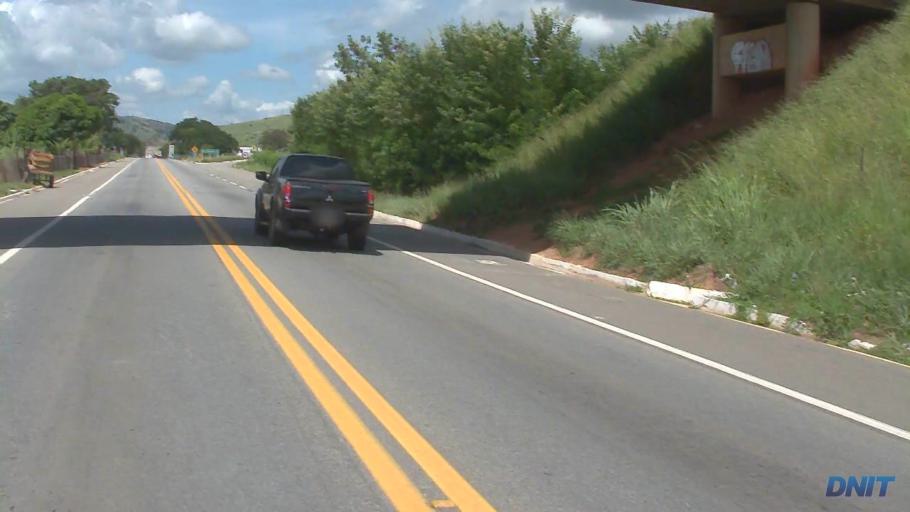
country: BR
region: Minas Gerais
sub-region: Governador Valadares
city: Governador Valadares
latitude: -18.9226
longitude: -42.0281
